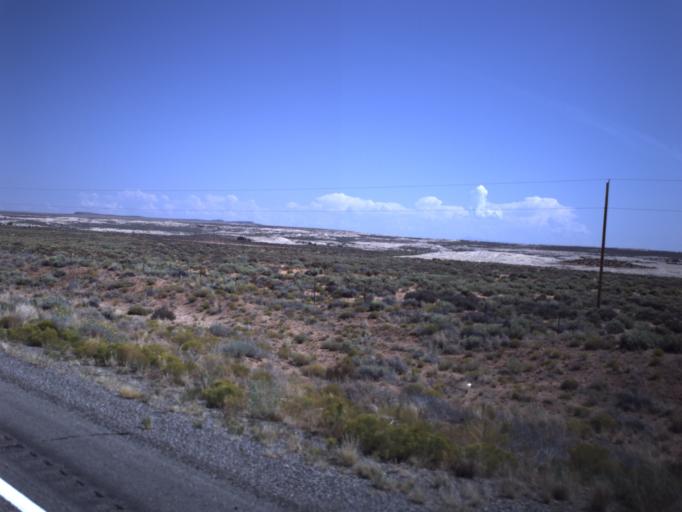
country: US
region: Utah
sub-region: San Juan County
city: Blanding
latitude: 37.0732
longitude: -109.5499
